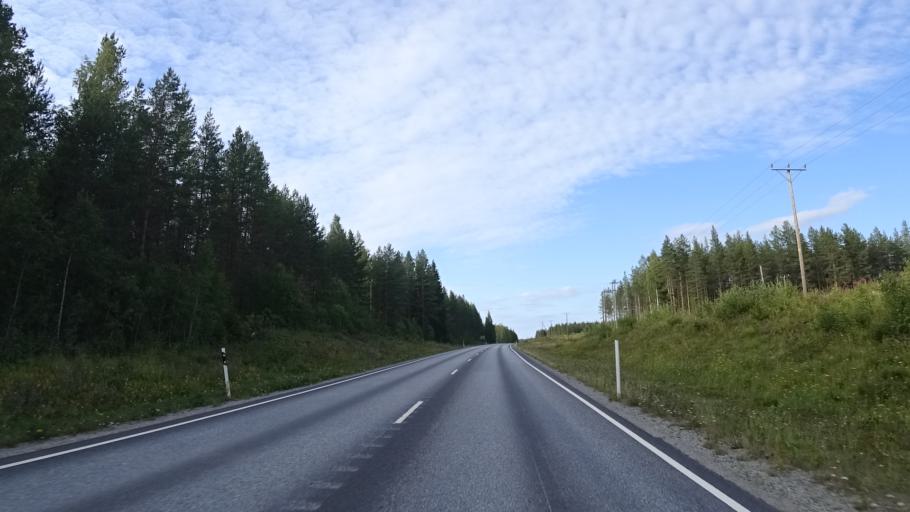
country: FI
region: North Karelia
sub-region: Joensuu
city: Eno
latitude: 62.8556
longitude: 30.1941
